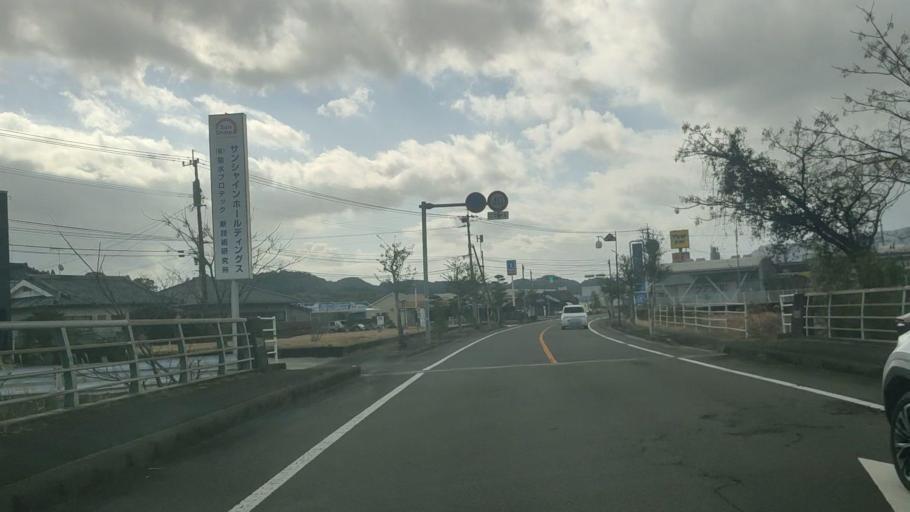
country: JP
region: Kagoshima
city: Okuchi-shinohara
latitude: 32.0507
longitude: 130.7740
